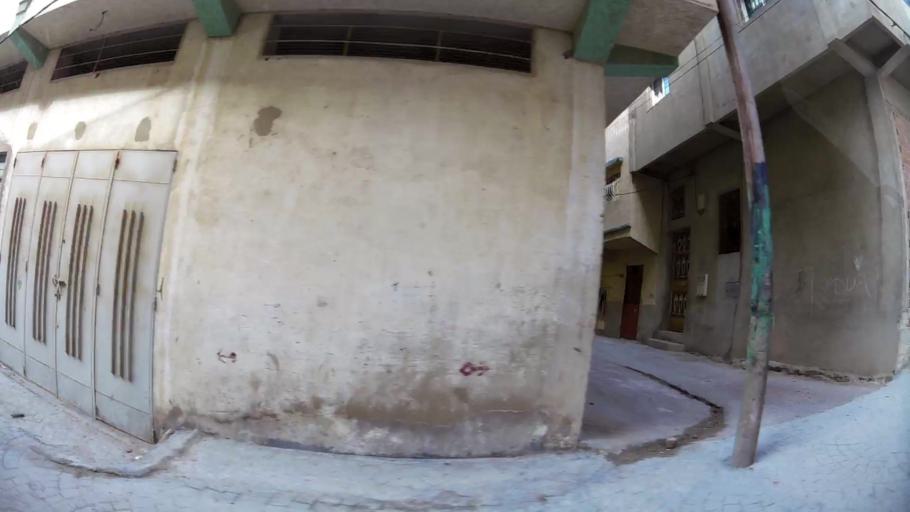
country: MA
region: Tanger-Tetouan
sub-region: Tanger-Assilah
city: Tangier
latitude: 35.7654
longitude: -5.7729
